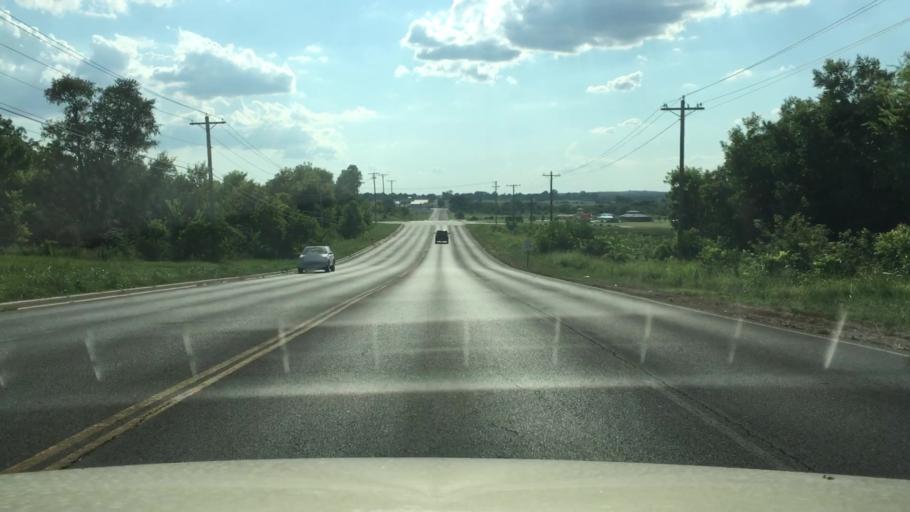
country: US
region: Oklahoma
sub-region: Cherokee County
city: Tahlequah
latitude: 35.9299
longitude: -94.9865
